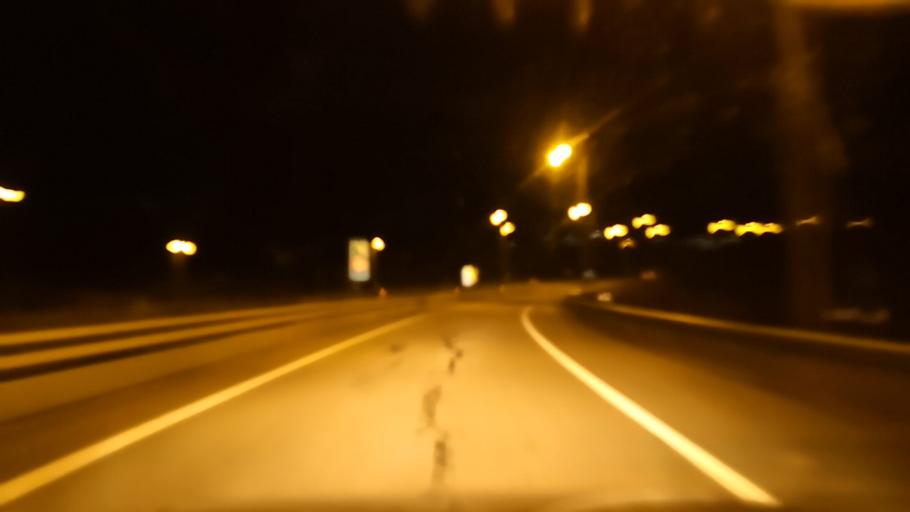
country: PT
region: Evora
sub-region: Estremoz
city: Estremoz
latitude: 38.8211
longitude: -7.6060
